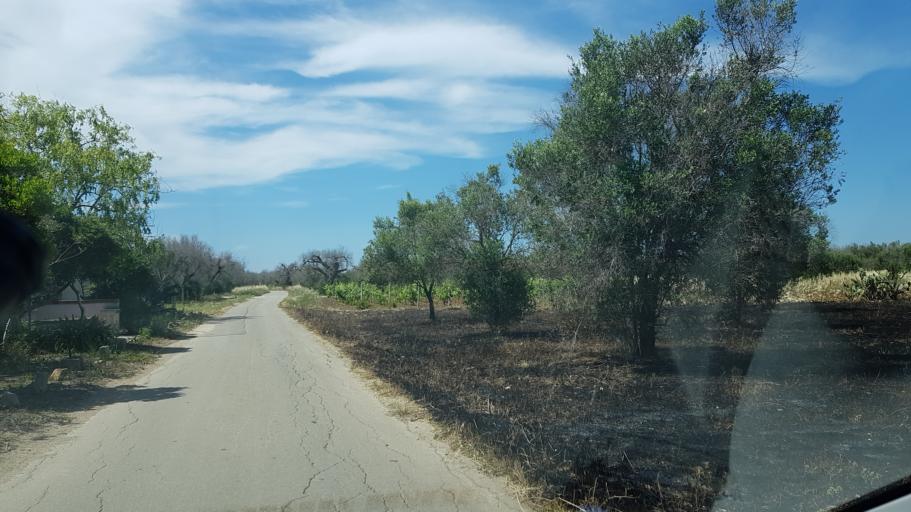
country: IT
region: Apulia
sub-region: Provincia di Brindisi
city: San Pietro Vernotico
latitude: 40.5243
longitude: 18.0098
